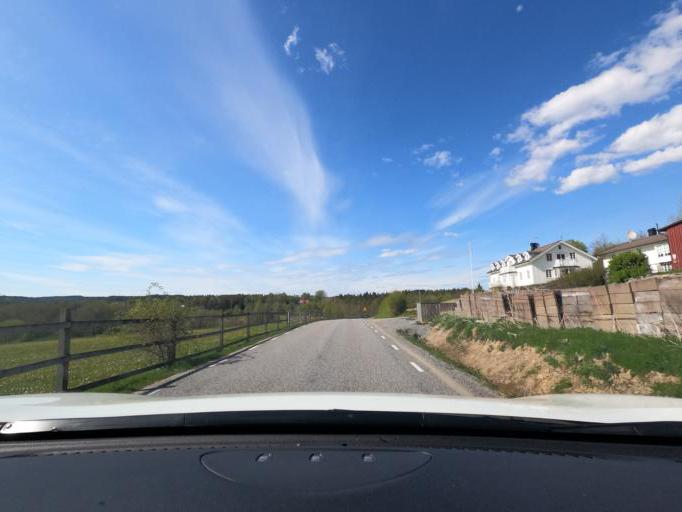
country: SE
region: Vaestra Goetaland
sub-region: Harryda Kommun
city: Ravlanda
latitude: 57.6420
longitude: 12.4970
